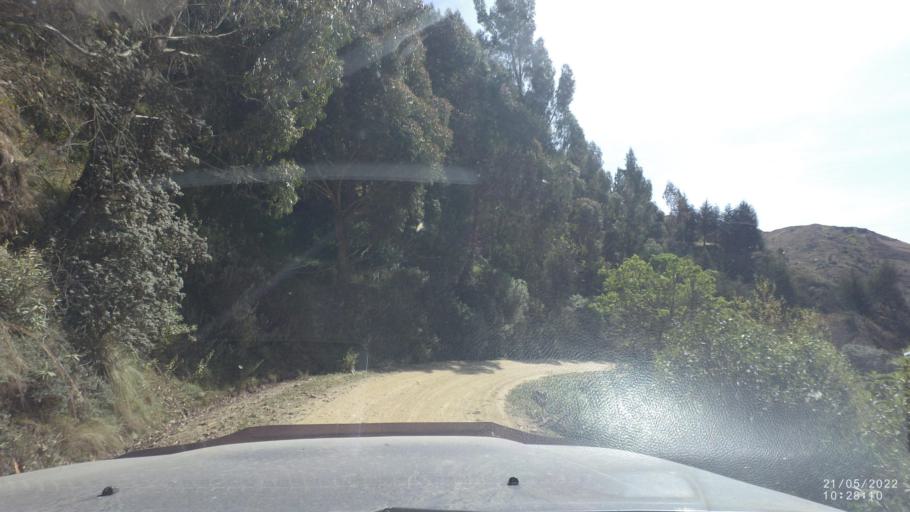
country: BO
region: Cochabamba
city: Colomi
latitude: -17.3223
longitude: -65.9424
